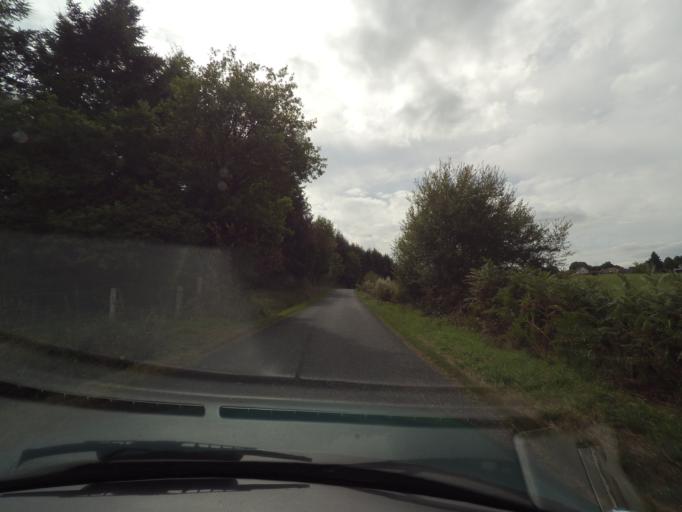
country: FR
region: Limousin
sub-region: Departement de la Haute-Vienne
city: Bussiere-Galant
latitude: 45.6442
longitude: 1.0942
